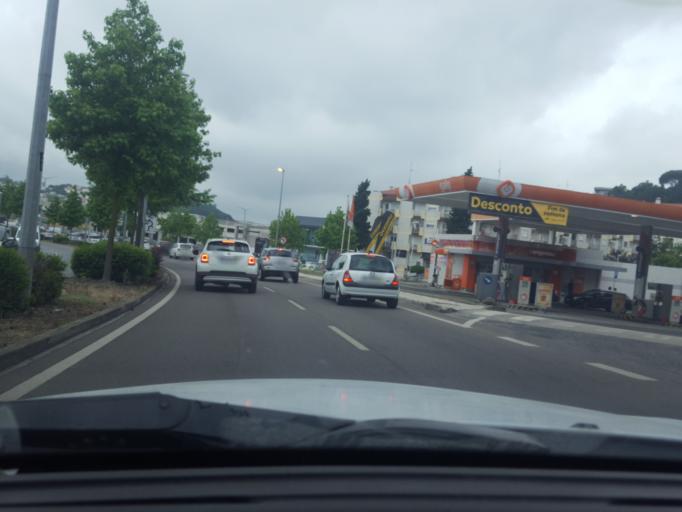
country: PT
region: Leiria
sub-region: Leiria
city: Leiria
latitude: 39.7386
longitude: -8.8149
